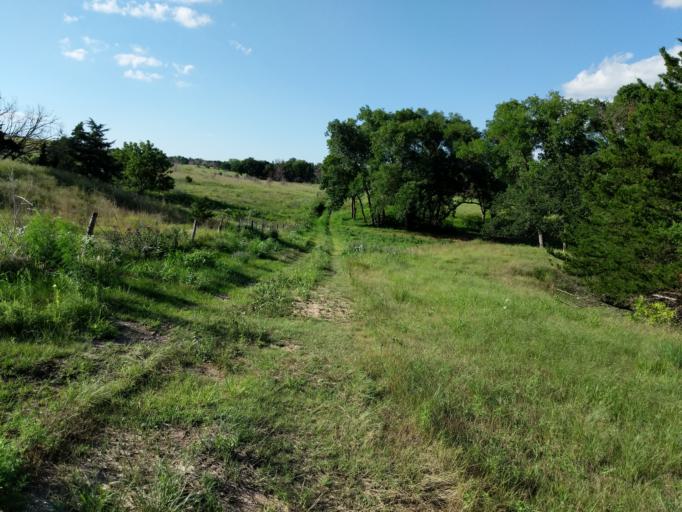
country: US
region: Kansas
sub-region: Smith County
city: Smith Center
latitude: 39.8908
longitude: -98.9498
